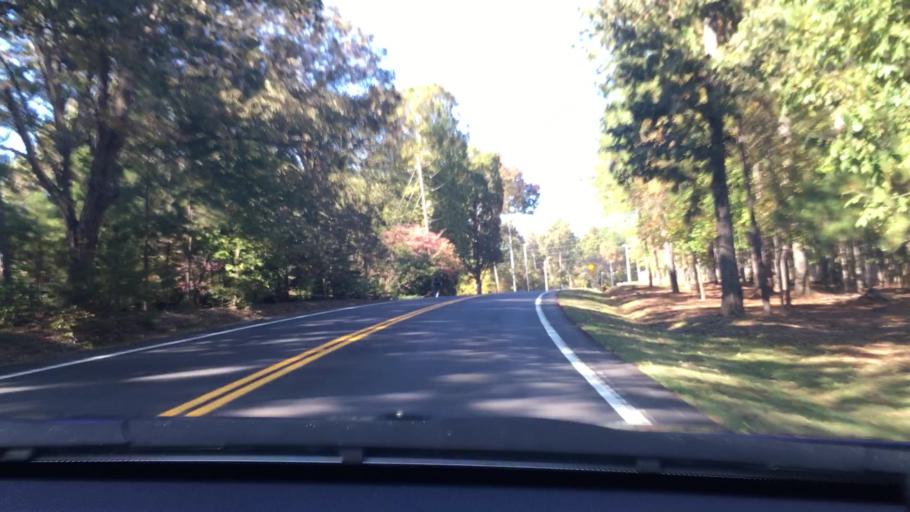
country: US
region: South Carolina
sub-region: Lexington County
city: Irmo
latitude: 34.1282
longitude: -81.1773
